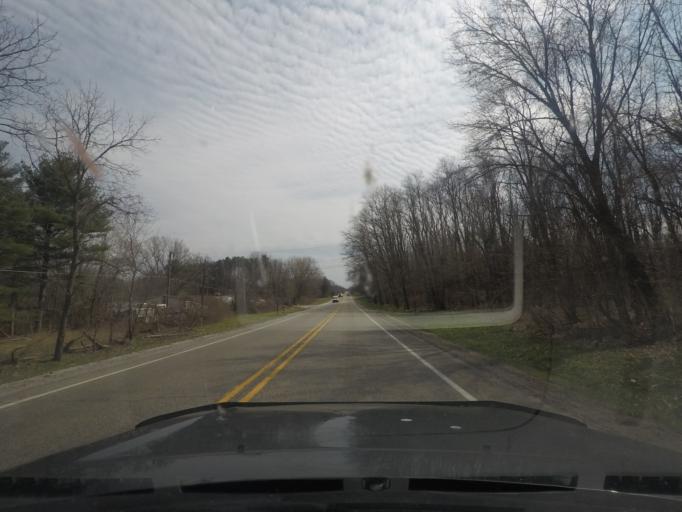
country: US
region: Indiana
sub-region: LaPorte County
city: Trail Creek
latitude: 41.6760
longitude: -86.7843
